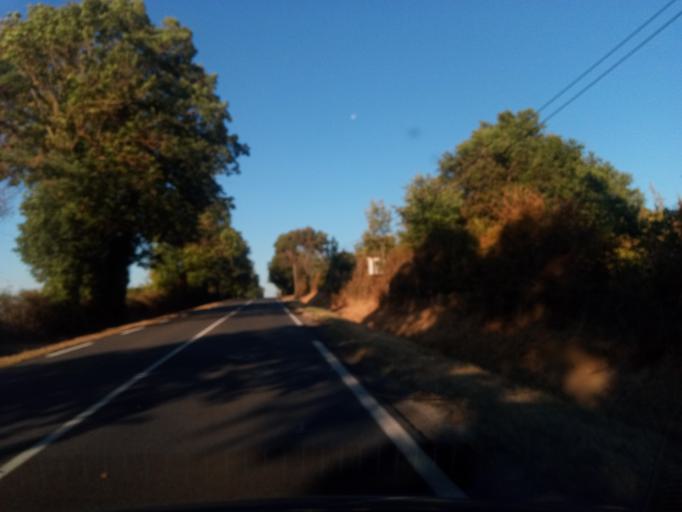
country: FR
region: Poitou-Charentes
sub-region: Departement de la Vienne
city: Montmorillon
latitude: 46.4156
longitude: 0.8364
